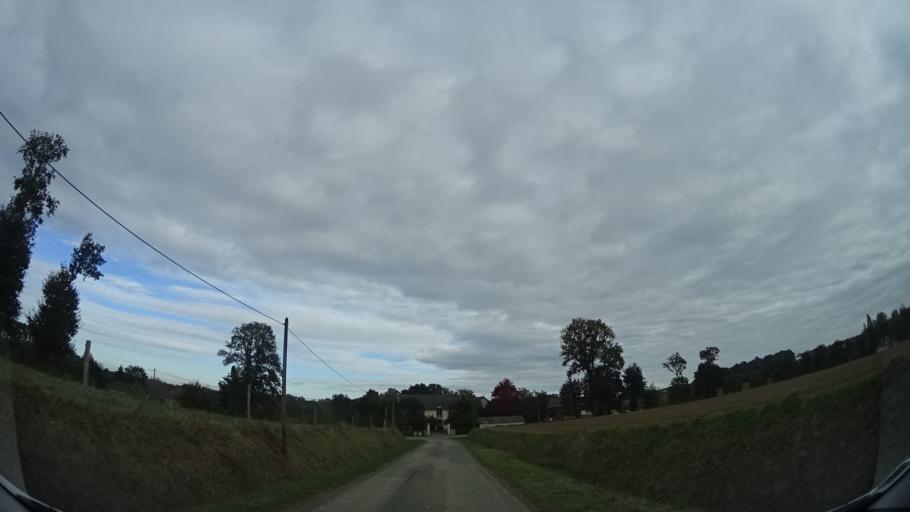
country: FR
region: Brittany
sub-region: Departement d'Ille-et-Vilaine
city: Vignoc
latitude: 48.2384
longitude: -1.7795
